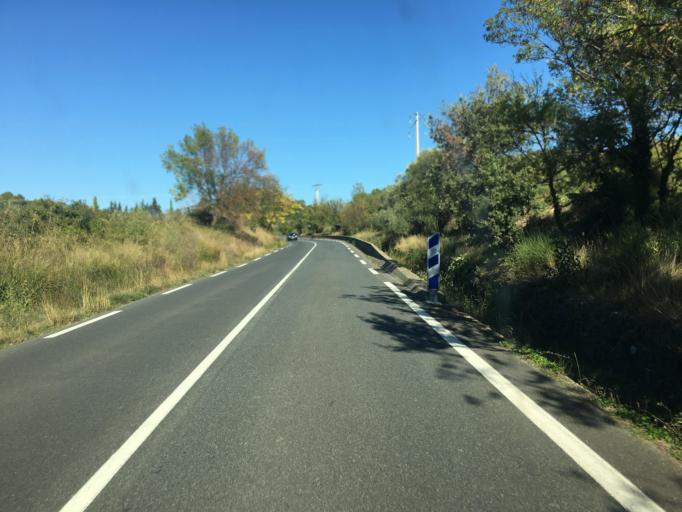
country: FR
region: Languedoc-Roussillon
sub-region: Departement de l'Herault
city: Nebian
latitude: 43.6130
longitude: 3.4065
